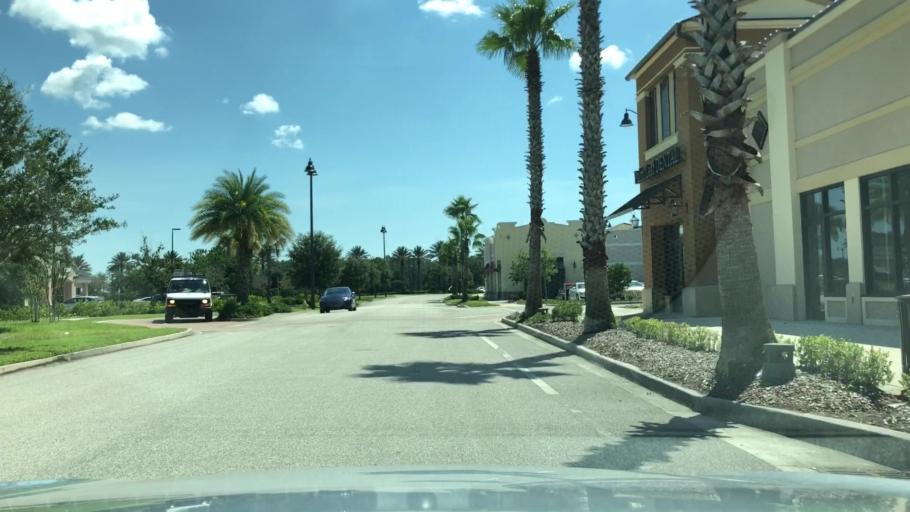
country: US
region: Florida
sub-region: Saint Johns County
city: Palm Valley
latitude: 30.1116
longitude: -81.4198
